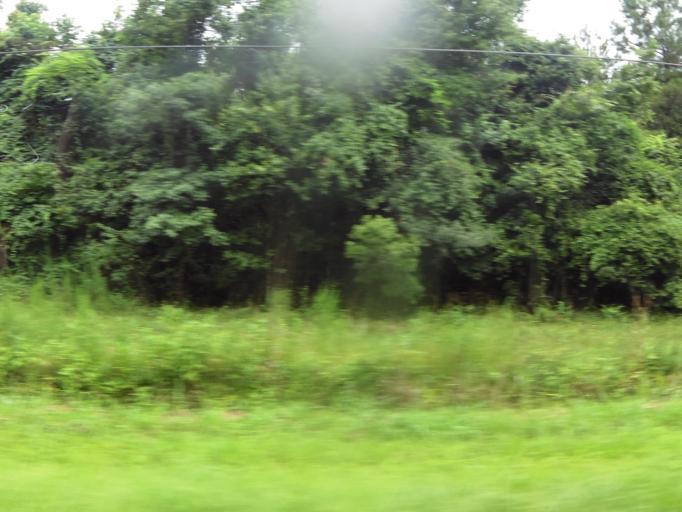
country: US
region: Florida
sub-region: Nassau County
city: Nassau Village-Ratliff
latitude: 30.4610
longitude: -81.7841
